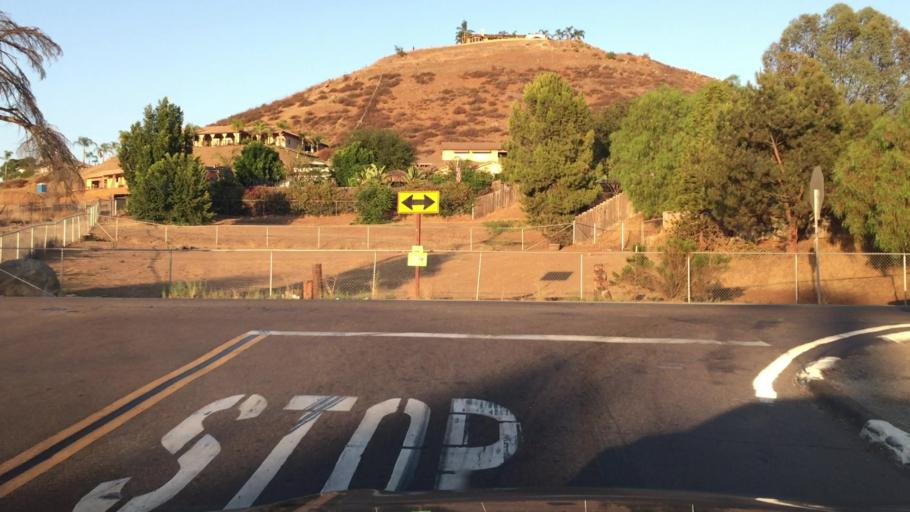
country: US
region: California
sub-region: San Diego County
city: Bostonia
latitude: 32.8190
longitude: -116.9447
